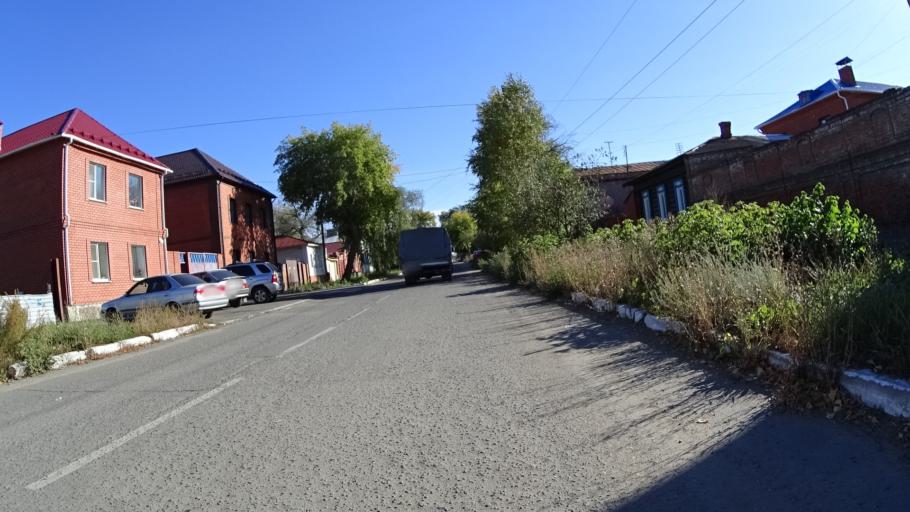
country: RU
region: Chelyabinsk
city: Troitsk
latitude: 54.0841
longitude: 61.5545
